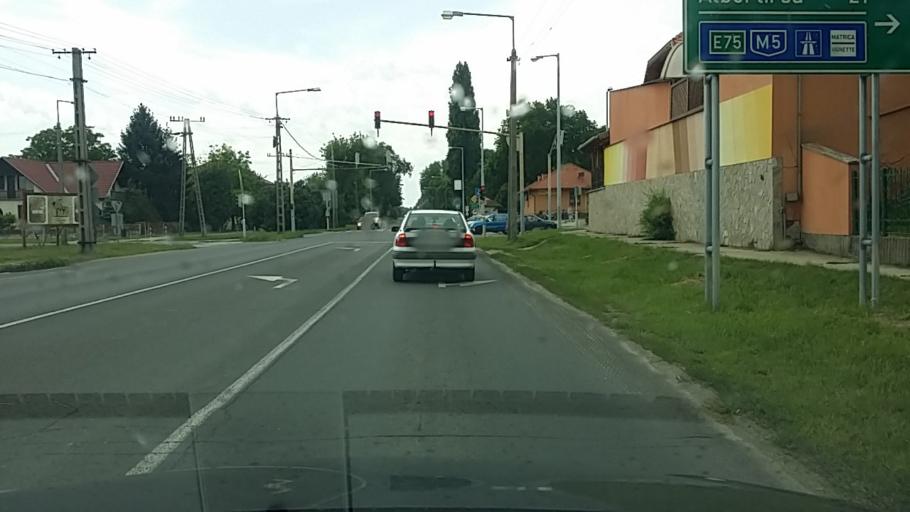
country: HU
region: Pest
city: Orkeny
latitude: 47.1270
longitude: 19.4286
